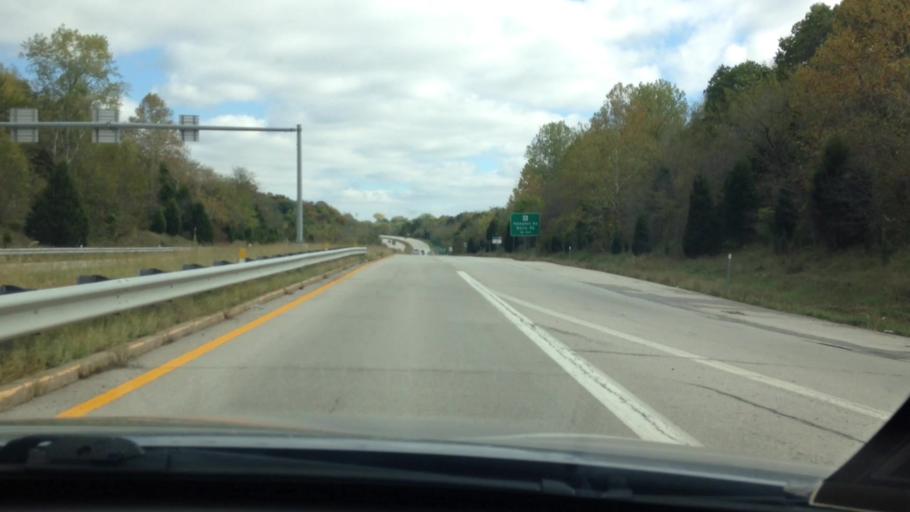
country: US
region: Missouri
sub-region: Platte County
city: Weatherby Lake
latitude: 39.2453
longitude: -94.7522
